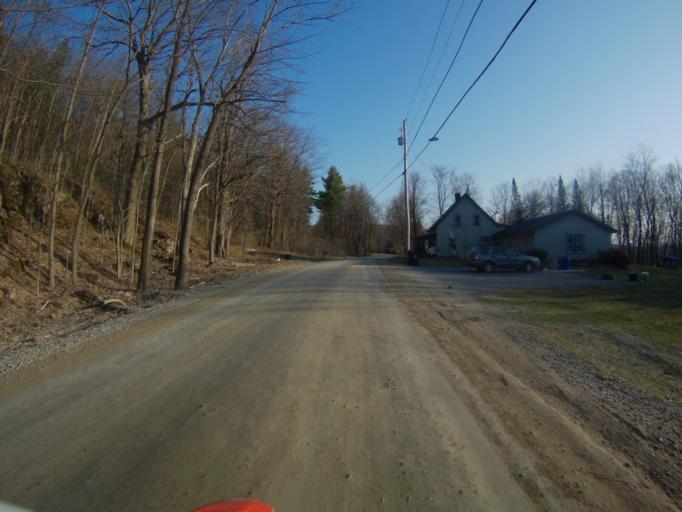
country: US
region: Vermont
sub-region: Addison County
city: Bristol
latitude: 44.1108
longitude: -73.0767
